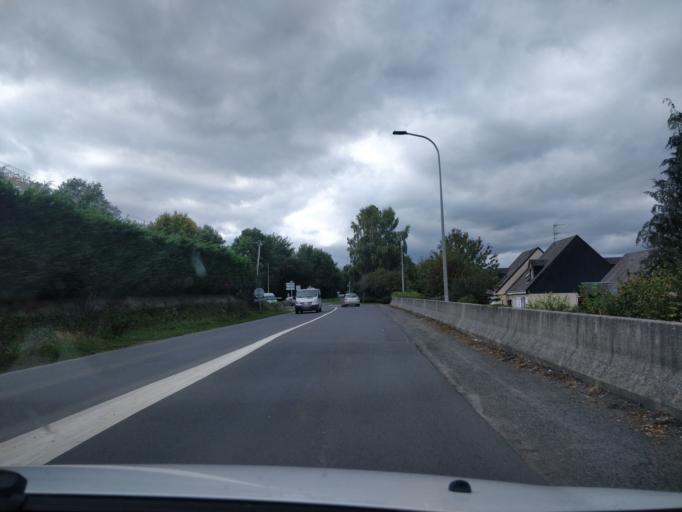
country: FR
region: Lower Normandy
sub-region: Departement du Calvados
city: Vire
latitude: 48.8455
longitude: -0.9058
